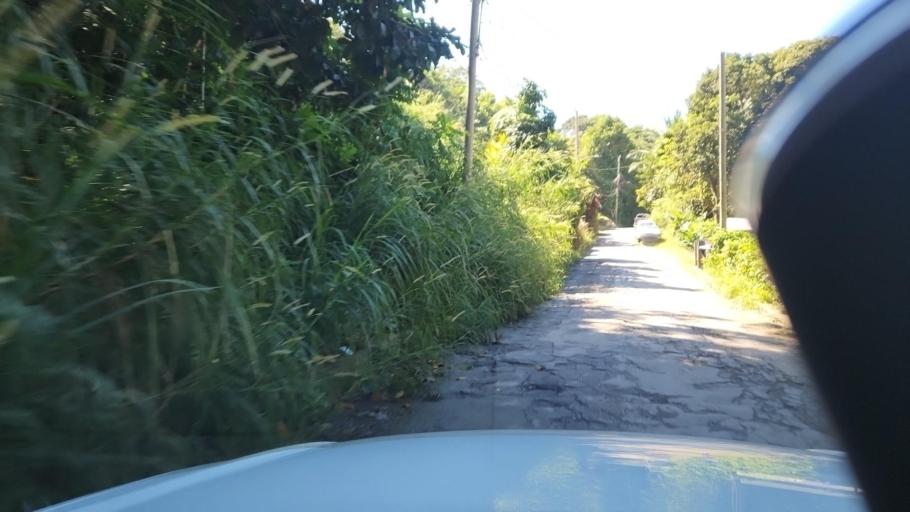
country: BB
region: Saint Thomas
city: Welchman Hall
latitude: 13.1953
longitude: -59.5749
